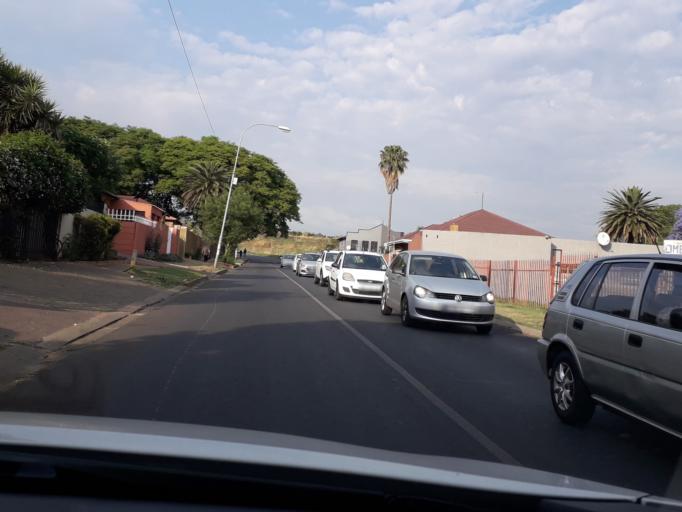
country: ZA
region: Gauteng
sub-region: City of Johannesburg Metropolitan Municipality
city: Johannesburg
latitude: -26.1665
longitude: 27.9770
